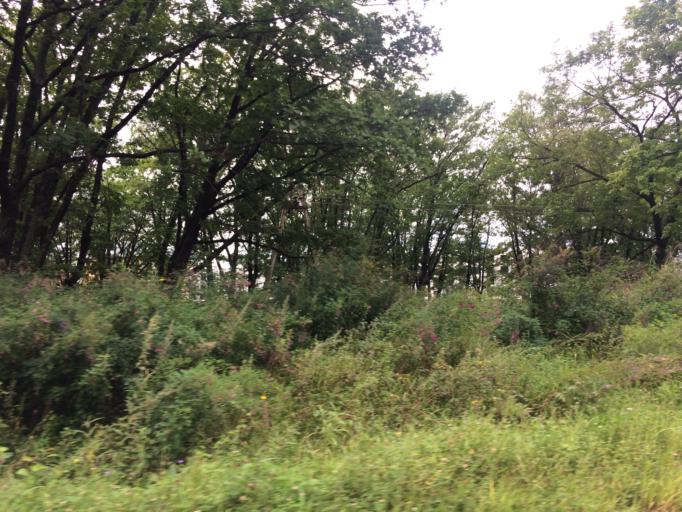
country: RU
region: Primorskiy
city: Lazo
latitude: 45.8231
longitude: 133.6439
